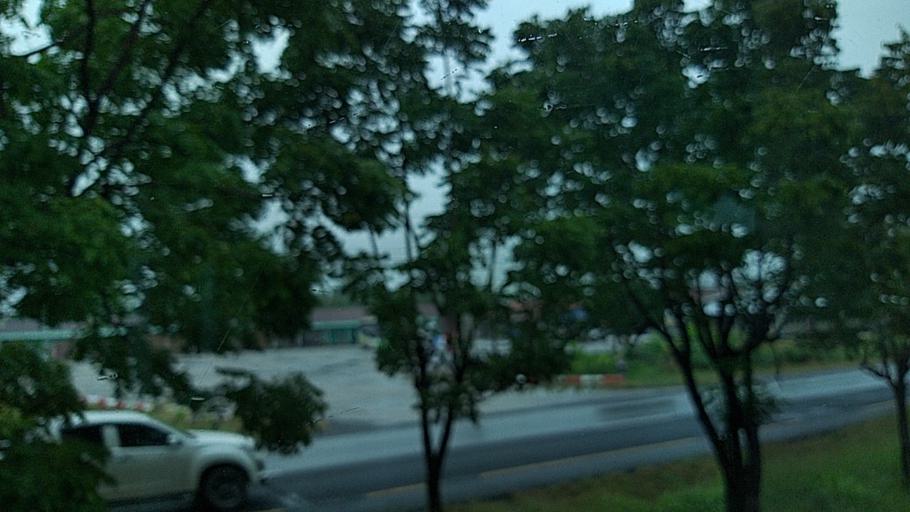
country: TH
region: Nakhon Ratchasima
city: Phimai
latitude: 15.2352
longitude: 102.3776
